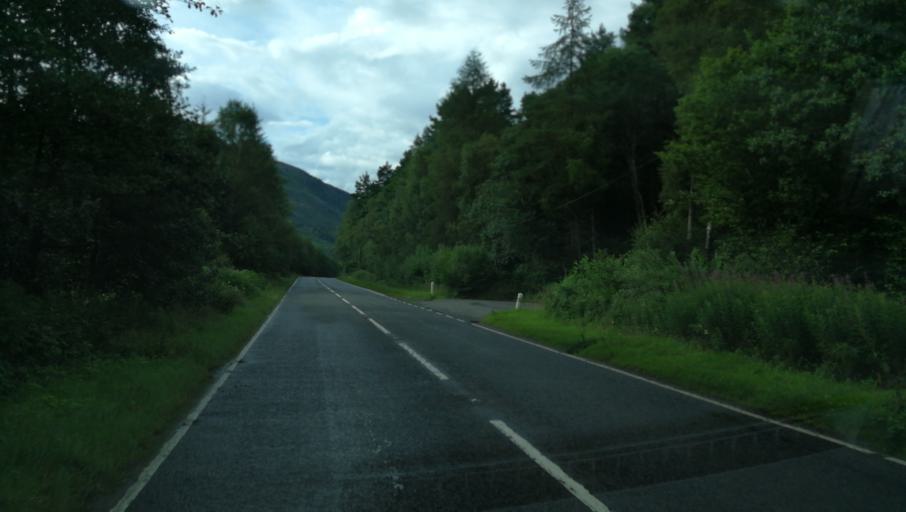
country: GB
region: Scotland
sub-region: Stirling
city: Callander
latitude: 56.3103
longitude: -4.3248
